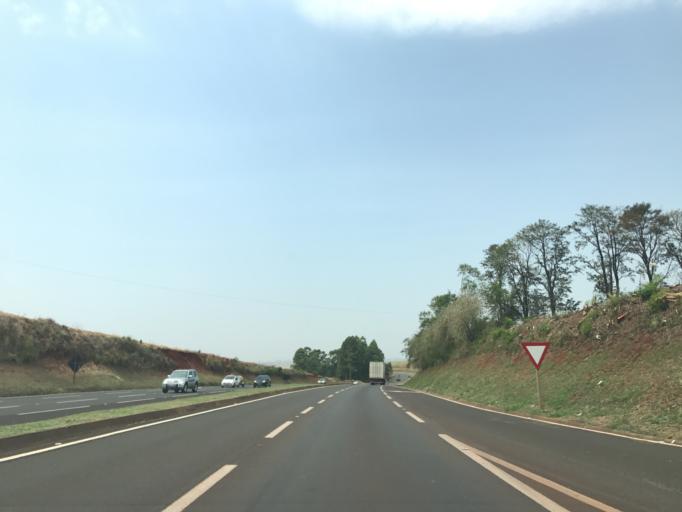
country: BR
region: Parana
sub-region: Rolandia
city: Rolandia
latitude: -23.3396
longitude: -51.3614
